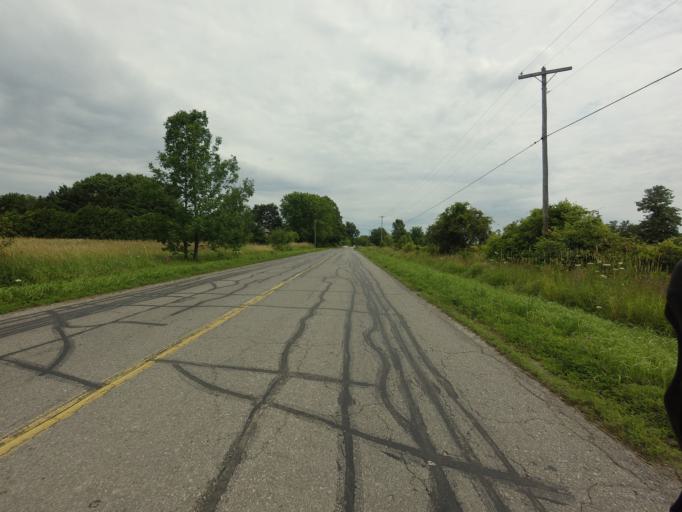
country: CA
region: Ontario
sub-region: Lanark County
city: Smiths Falls
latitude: 45.0130
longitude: -75.7287
